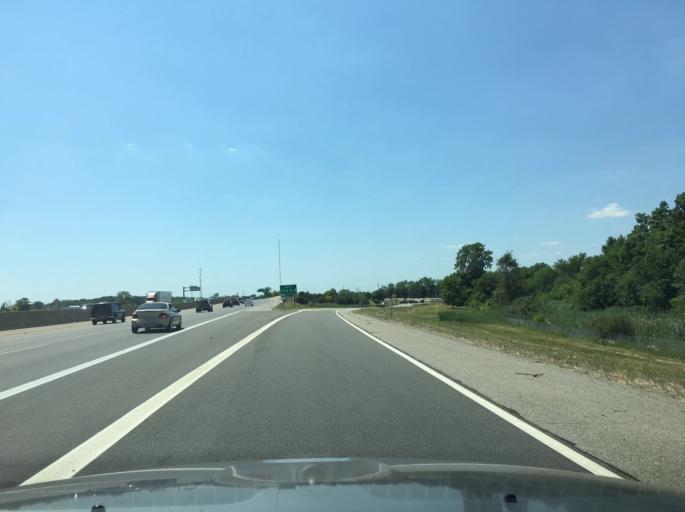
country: US
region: Michigan
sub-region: Macomb County
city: Mount Clemens
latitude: 42.5535
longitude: -82.8670
